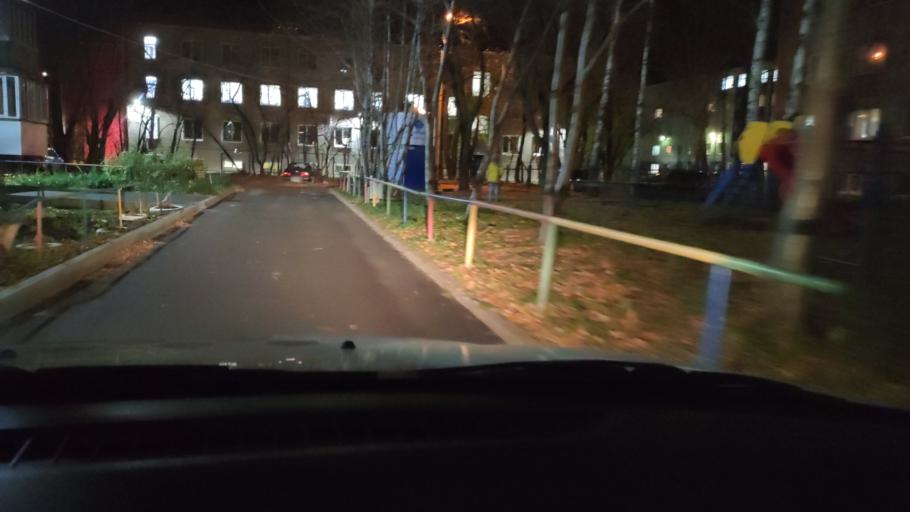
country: RU
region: Perm
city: Perm
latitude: 58.0154
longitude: 56.2765
